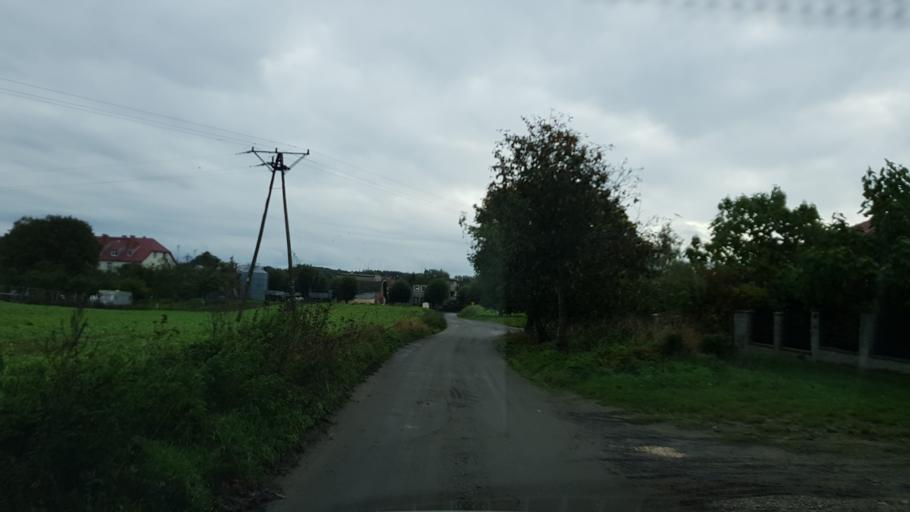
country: PL
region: West Pomeranian Voivodeship
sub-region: Powiat kamienski
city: Wolin
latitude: 53.8366
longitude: 14.6058
